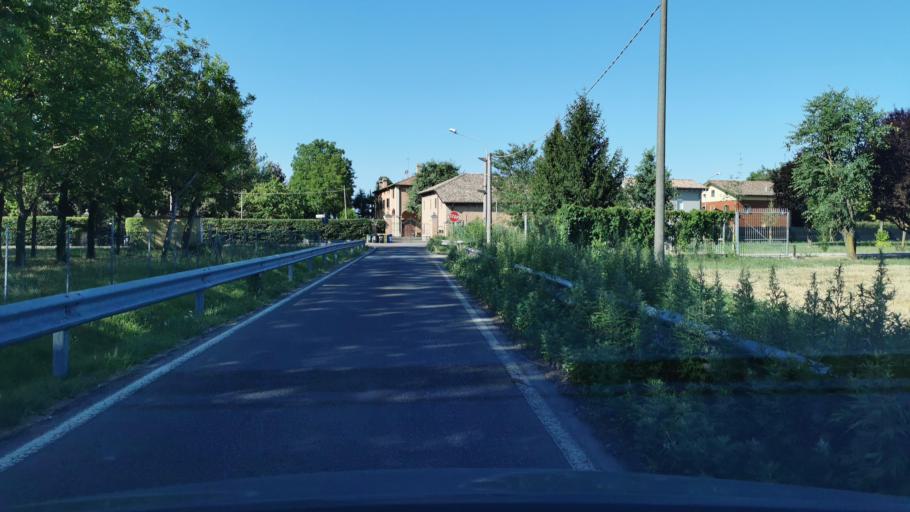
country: IT
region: Emilia-Romagna
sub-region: Provincia di Modena
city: Modena
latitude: 44.6190
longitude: 10.9036
